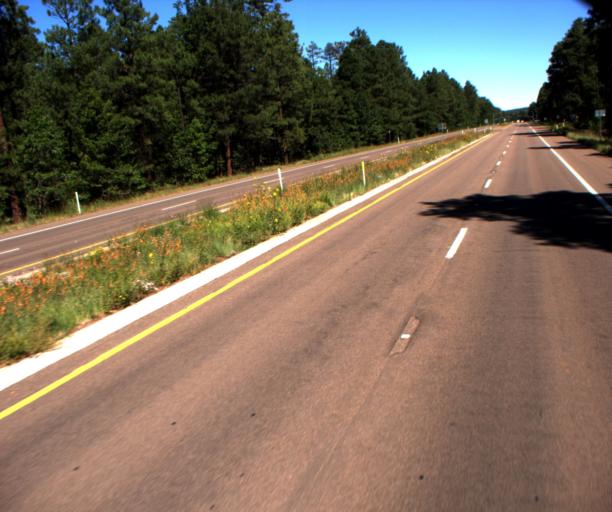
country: US
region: Arizona
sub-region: Navajo County
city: Pinetop-Lakeside
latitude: 34.1102
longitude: -109.9130
